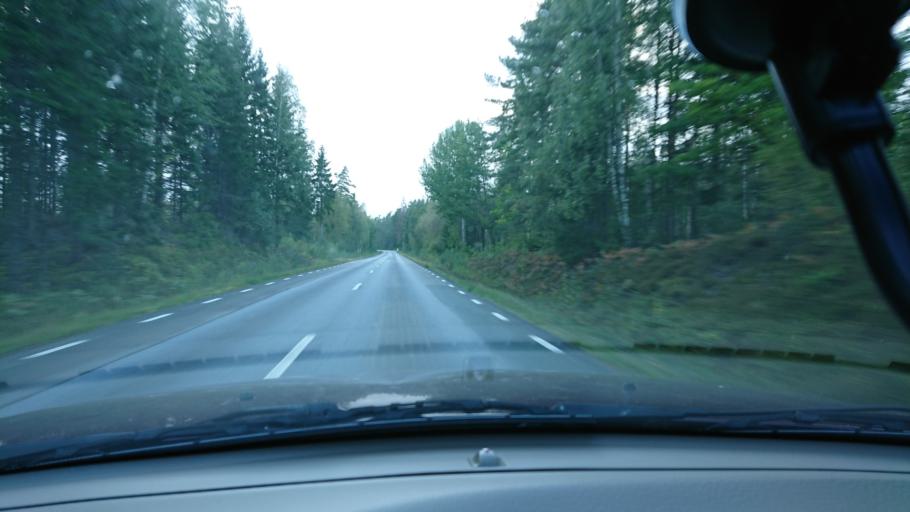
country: SE
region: Kronoberg
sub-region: Vaxjo Kommun
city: Rottne
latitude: 57.0658
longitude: 14.7455
